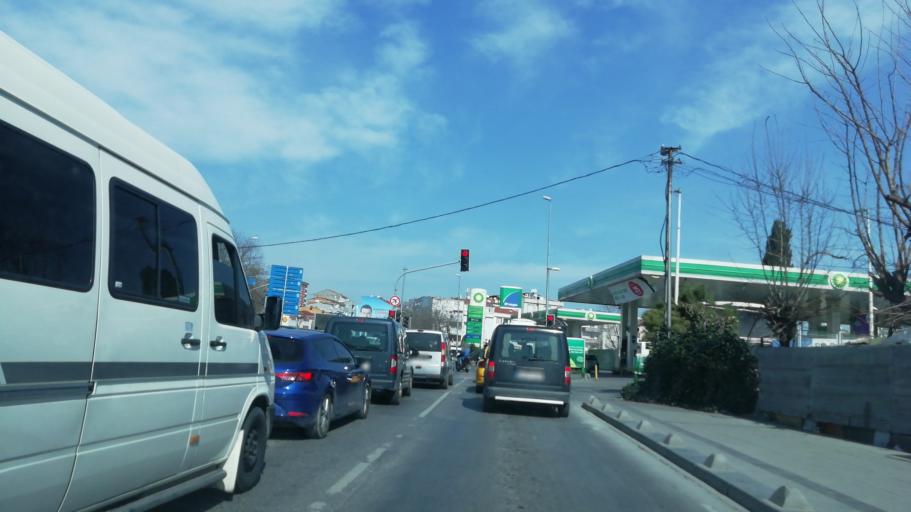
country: TR
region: Istanbul
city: Bagcilar
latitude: 41.0270
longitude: 28.8473
